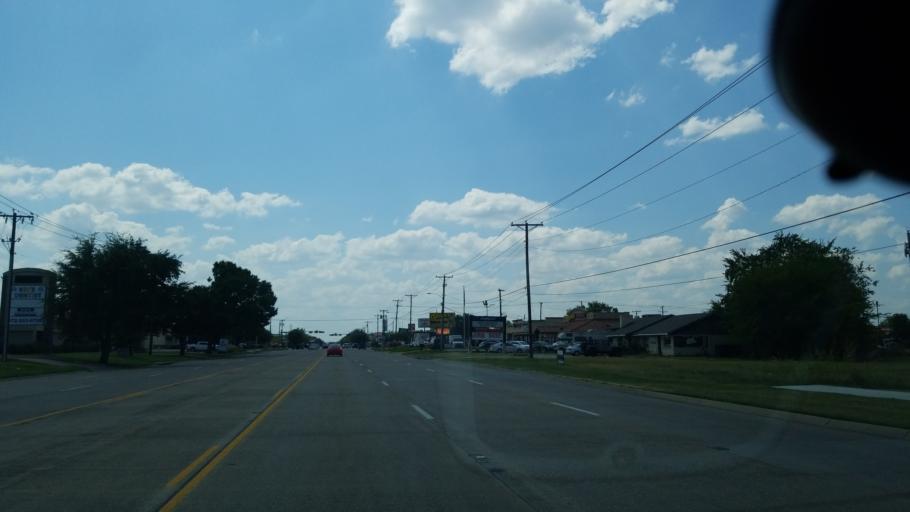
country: US
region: Texas
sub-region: Dallas County
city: Grand Prairie
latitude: 32.7120
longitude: -96.9942
